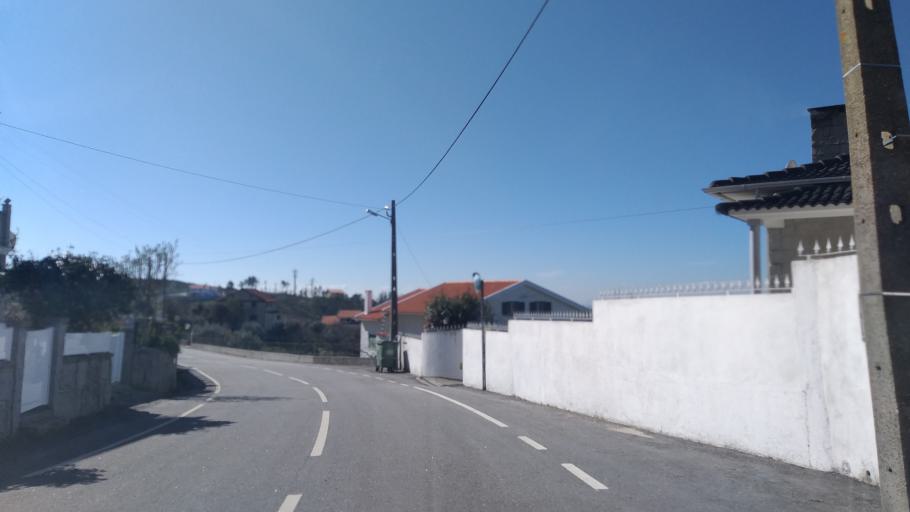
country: PT
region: Guarda
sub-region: Manteigas
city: Manteigas
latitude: 40.4686
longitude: -7.6191
